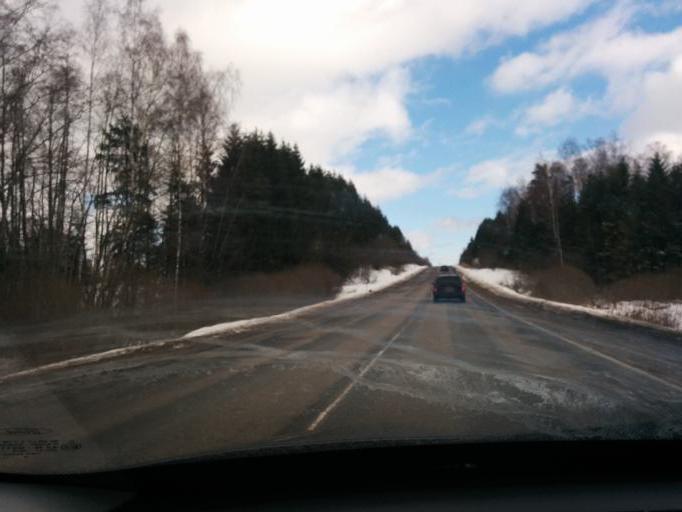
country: LV
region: Raunas
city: Rauna
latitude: 57.2824
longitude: 25.5058
